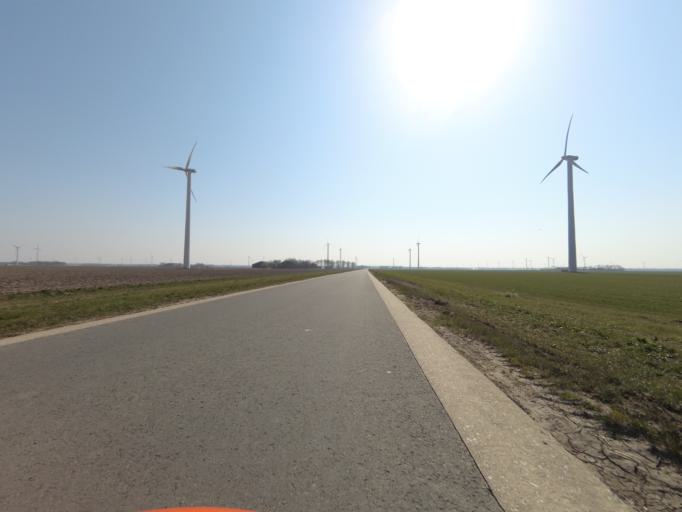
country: NL
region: Utrecht
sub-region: Gemeente Bunschoten
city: Spakenburg
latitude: 52.3401
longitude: 5.3799
